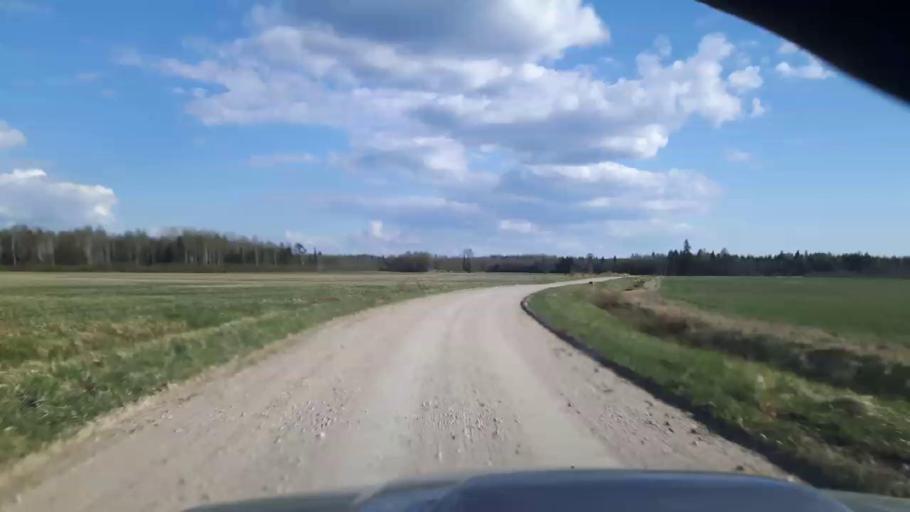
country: EE
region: Paernumaa
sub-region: Tootsi vald
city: Tootsi
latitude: 58.4386
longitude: 24.8557
